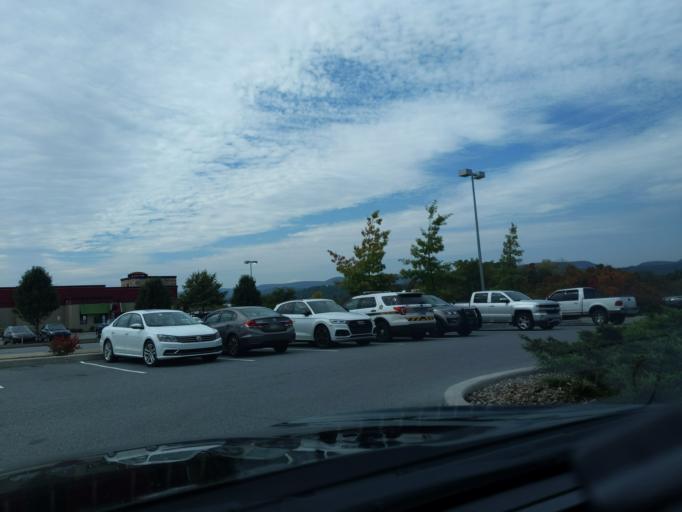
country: US
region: Pennsylvania
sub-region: Blair County
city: Lakemont
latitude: 40.4885
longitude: -78.3866
